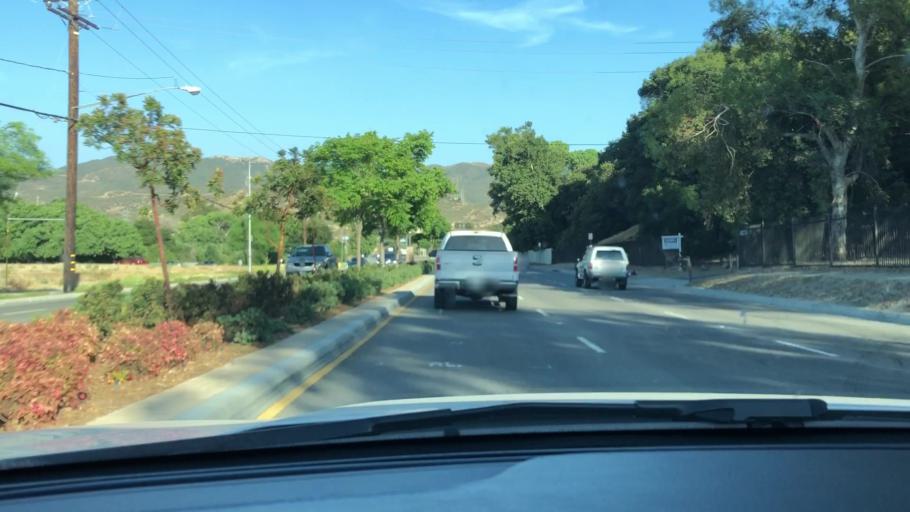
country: US
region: California
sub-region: Los Angeles County
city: Santa Clarita
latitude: 34.3674
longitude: -118.5093
